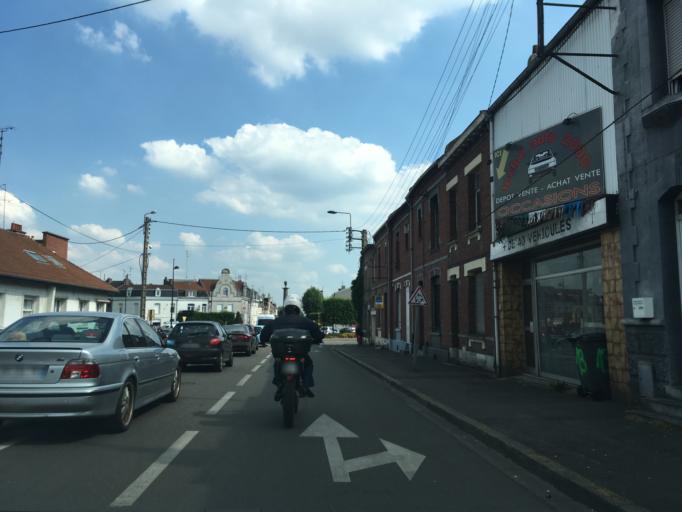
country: FR
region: Nord-Pas-de-Calais
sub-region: Departement du Nord
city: Anzin
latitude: 50.3573
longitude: 3.5035
